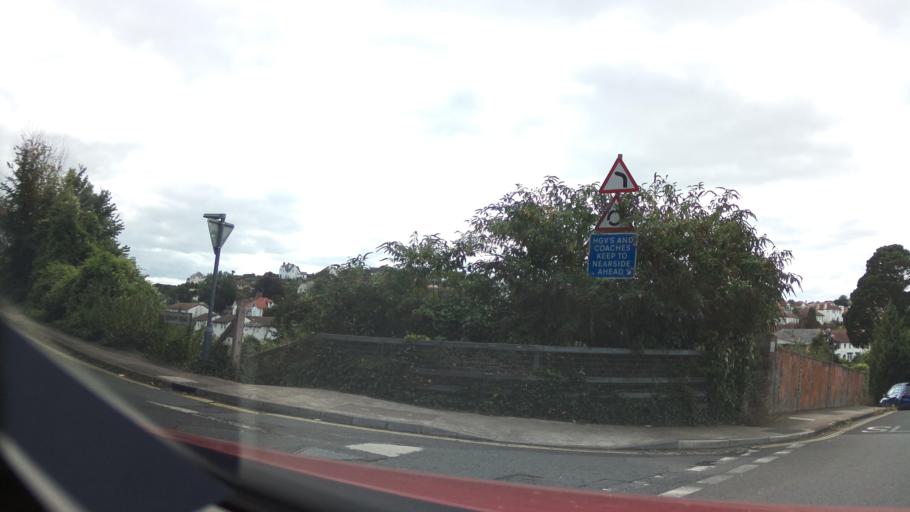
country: GB
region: England
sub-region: Borough of Torbay
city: Paignton
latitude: 50.4307
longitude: -3.5647
